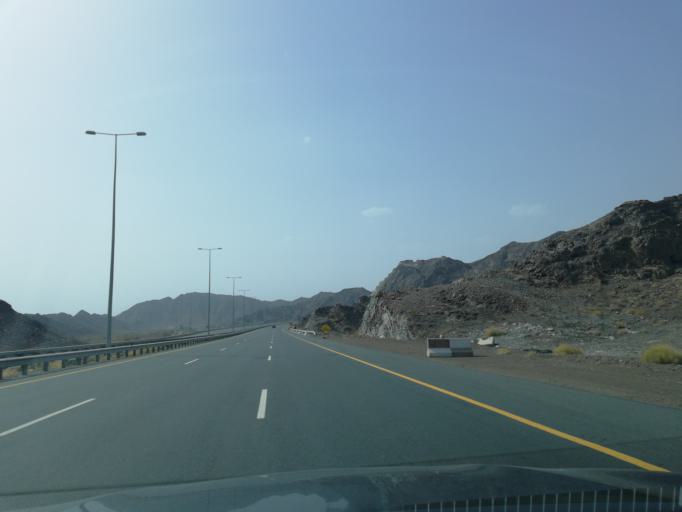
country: OM
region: Muhafazat ad Dakhiliyah
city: Sufalat Sama'il
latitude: 22.9750
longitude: 58.2370
